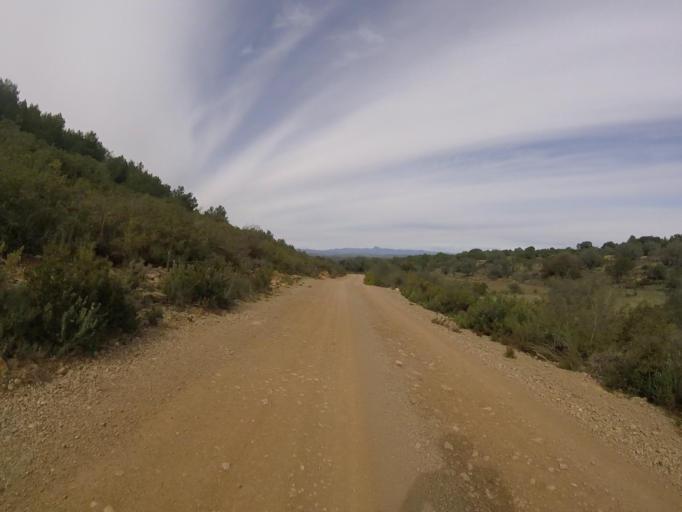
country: ES
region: Valencia
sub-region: Provincia de Castello
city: Cabanes
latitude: 40.1950
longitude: 0.0805
